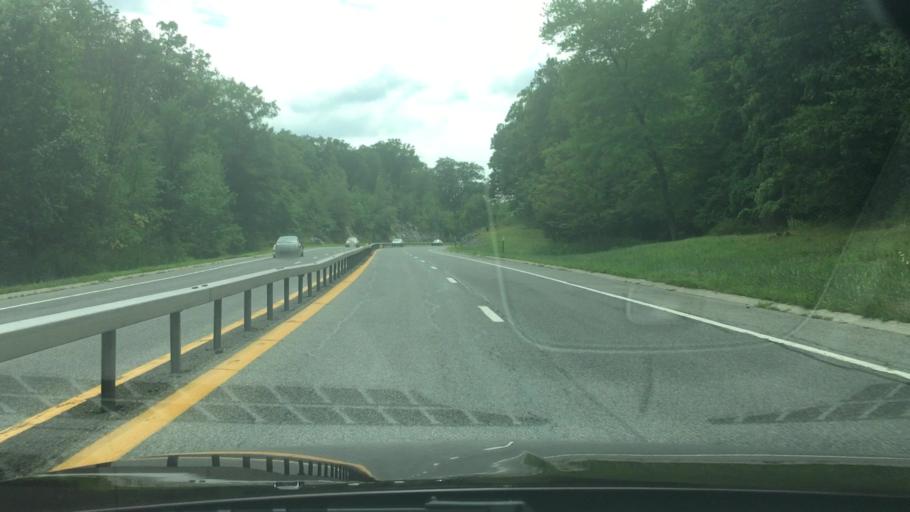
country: US
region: New York
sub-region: Dutchess County
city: Brinckerhoff
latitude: 41.4875
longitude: -73.8093
